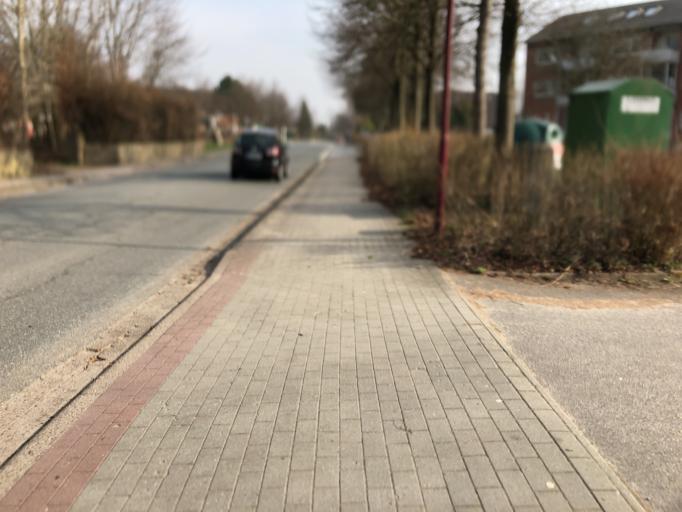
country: DE
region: Schleswig-Holstein
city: Tarp
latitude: 54.6662
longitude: 9.4073
